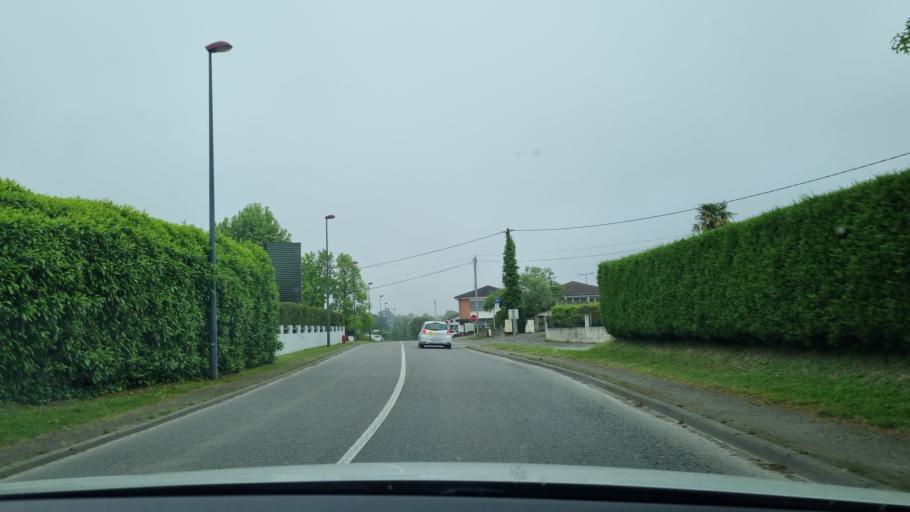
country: FR
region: Aquitaine
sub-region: Departement des Pyrenees-Atlantiques
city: Orthez
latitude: 43.4810
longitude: -0.7653
